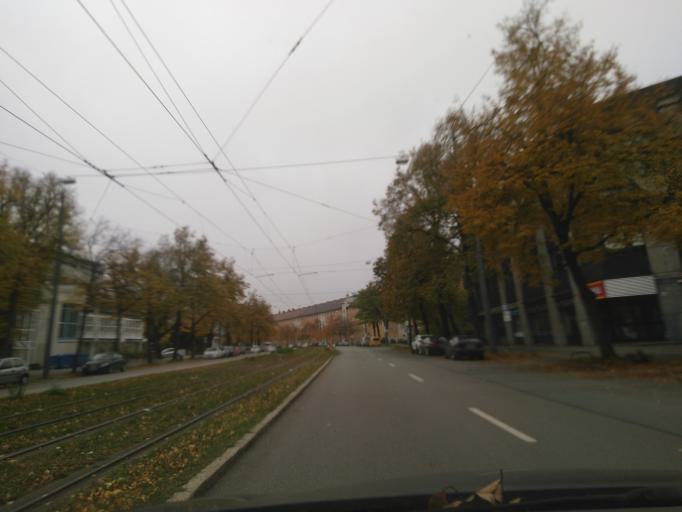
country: DE
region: Bavaria
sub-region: Upper Bavaria
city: Munich
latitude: 48.1136
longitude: 11.5927
